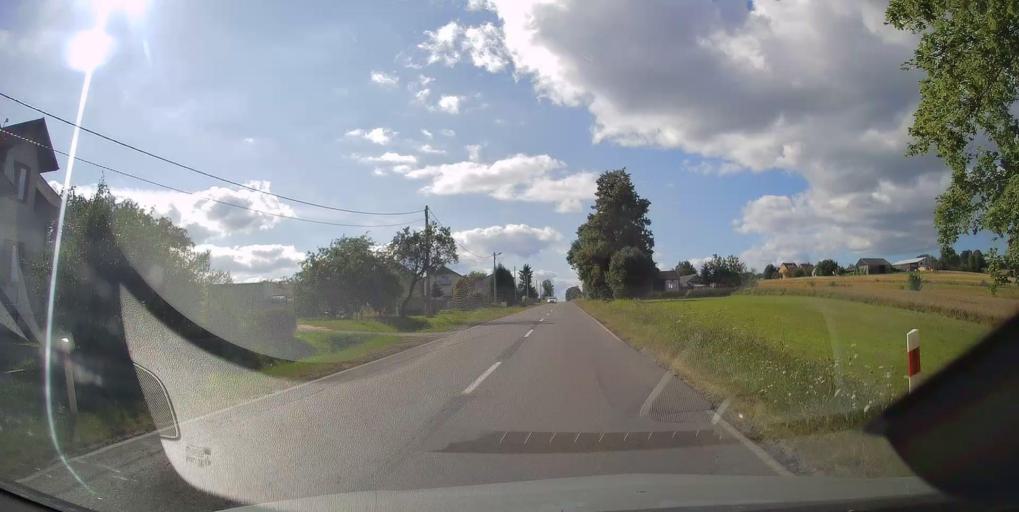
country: PL
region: Swietokrzyskie
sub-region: Powiat kielecki
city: Bodzentyn
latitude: 50.9689
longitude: 20.8856
